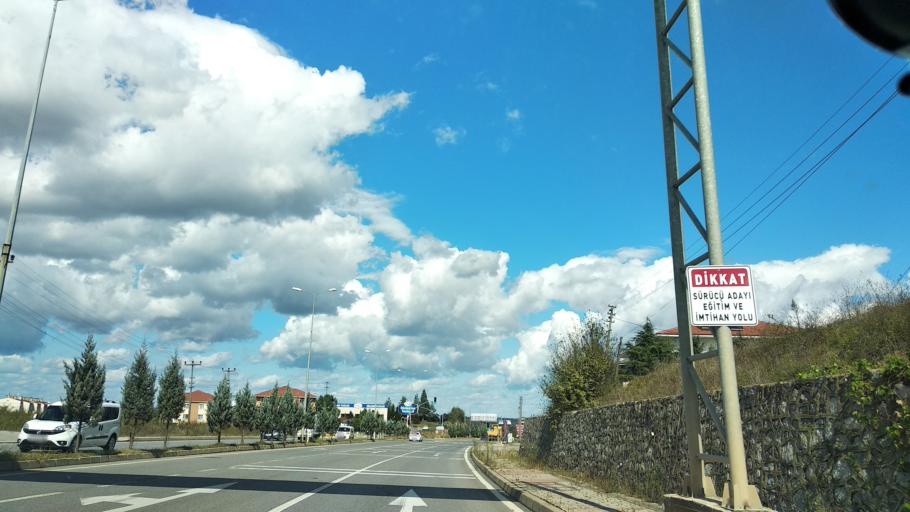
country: TR
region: Sakarya
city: Ferizli
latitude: 40.9500
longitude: 30.4991
